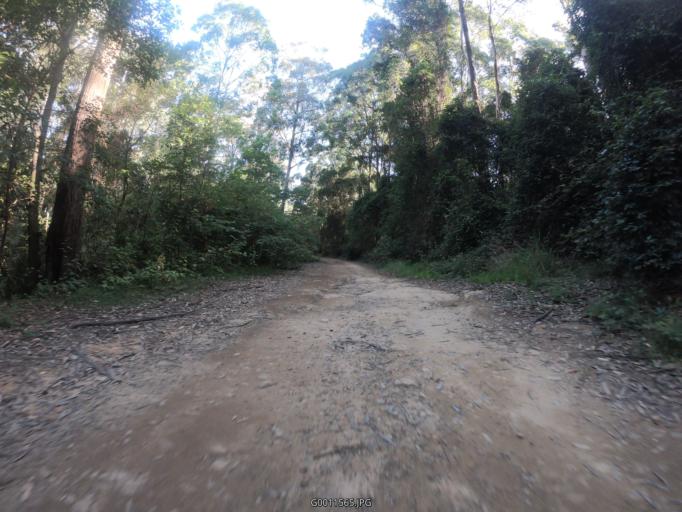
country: AU
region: New South Wales
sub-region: Lake Macquarie Shire
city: Cooranbong
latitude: -33.0415
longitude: 151.3026
